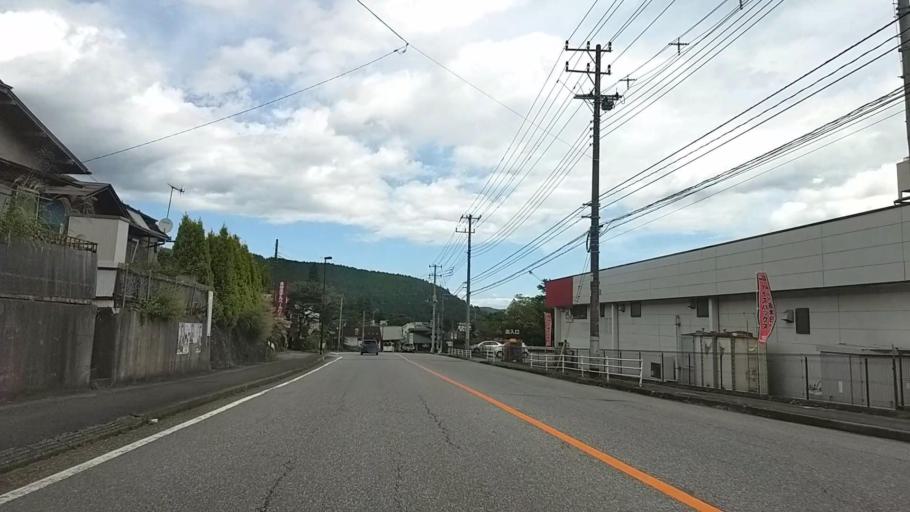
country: JP
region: Tochigi
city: Nikko
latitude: 36.7496
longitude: 139.5776
